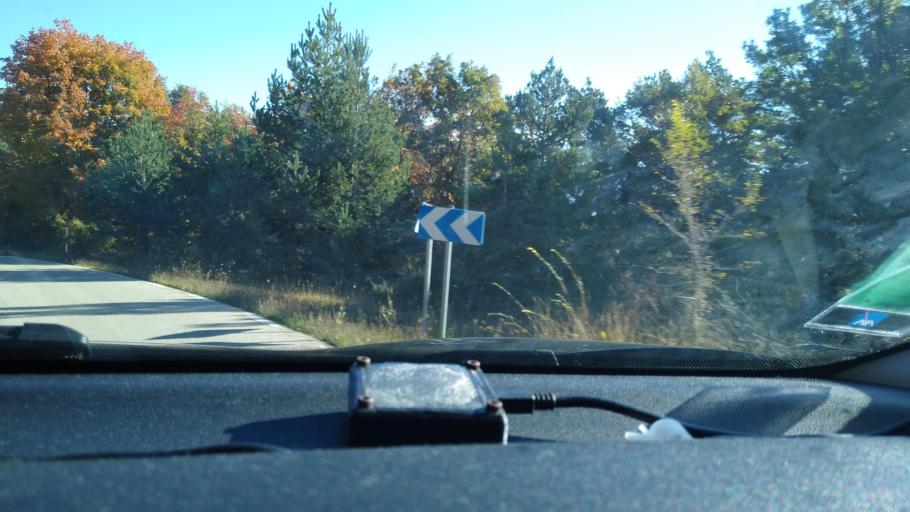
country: ES
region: Catalonia
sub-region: Provincia de Barcelona
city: Vallcebre
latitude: 42.1829
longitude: 1.8251
